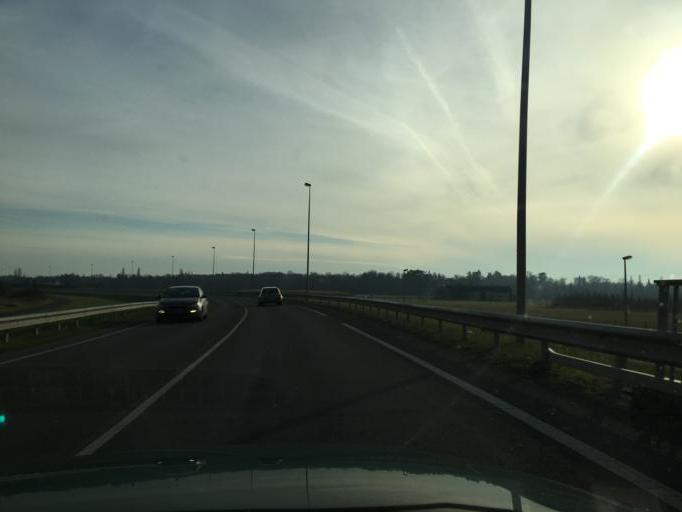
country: FR
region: Centre
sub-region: Departement du Loiret
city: Saint-Denis-en-Val
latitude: 47.8589
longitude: 1.9366
